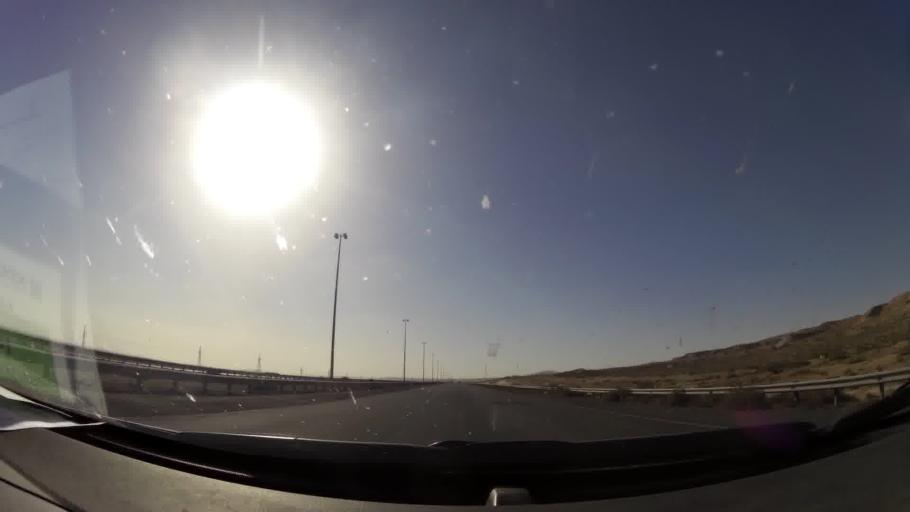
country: KW
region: Al Asimah
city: Kuwait City
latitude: 29.5430
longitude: 47.8578
